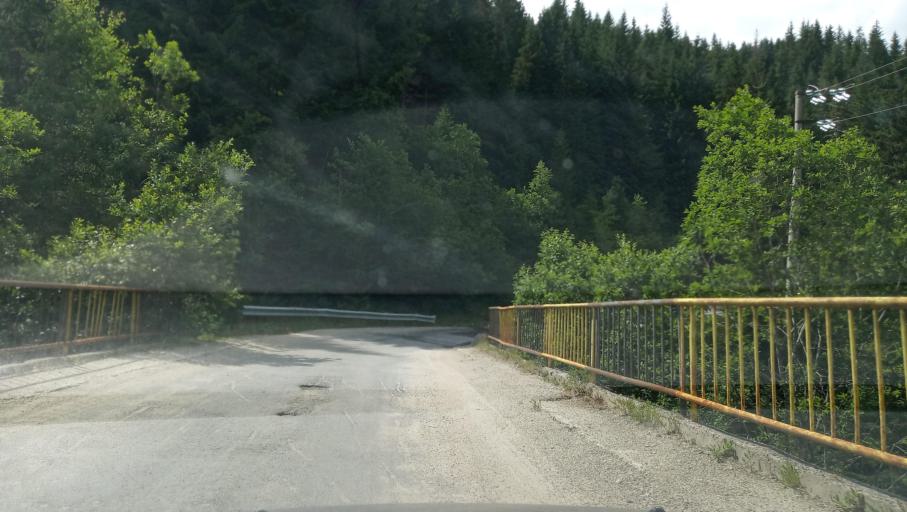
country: RO
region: Dambovita
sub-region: Comuna Moroeni
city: Glod
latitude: 45.3356
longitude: 25.4252
